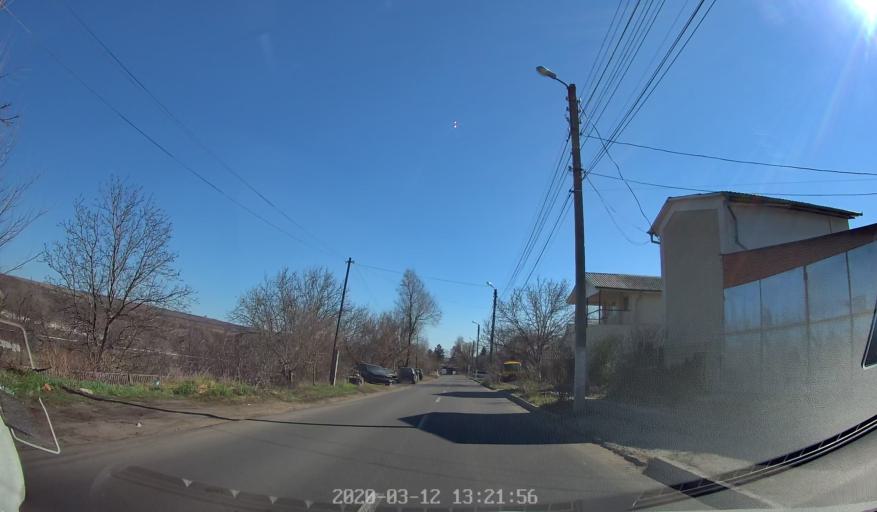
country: MD
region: Laloveni
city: Ialoveni
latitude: 46.9490
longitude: 28.8348
